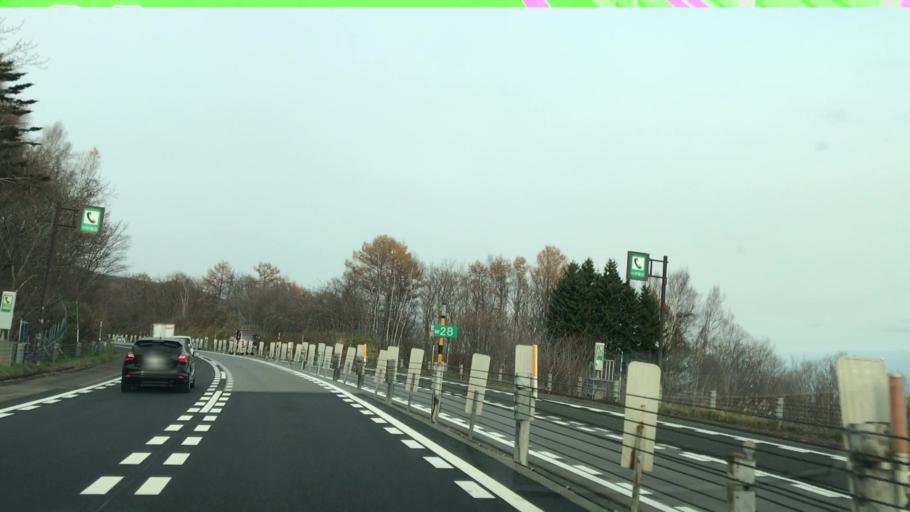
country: JP
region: Hokkaido
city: Otaru
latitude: 43.1513
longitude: 141.1269
